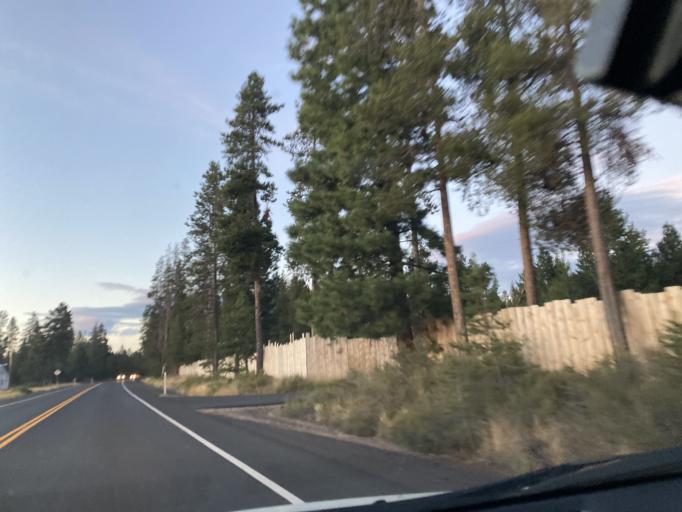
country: US
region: Oregon
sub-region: Deschutes County
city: Three Rivers
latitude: 43.8251
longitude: -121.4425
